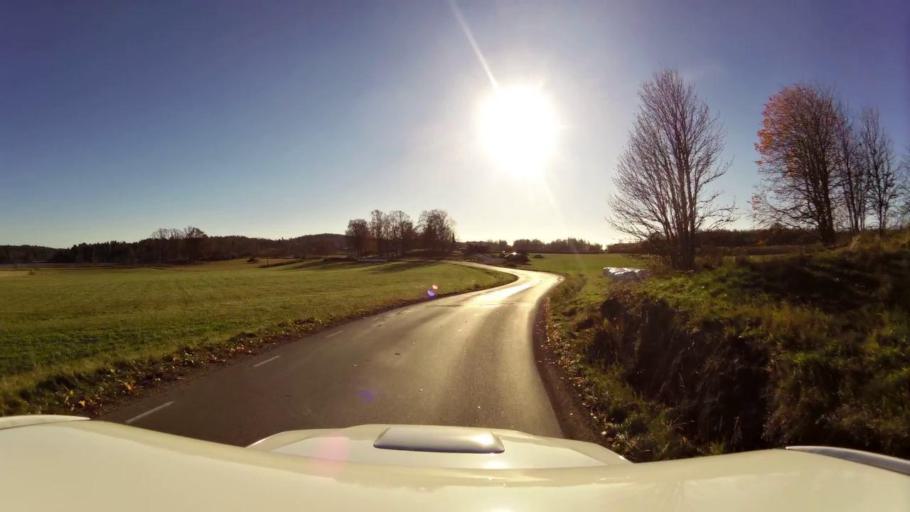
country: SE
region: OEstergoetland
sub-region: Kinda Kommun
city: Rimforsa
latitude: 58.2349
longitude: 15.6899
